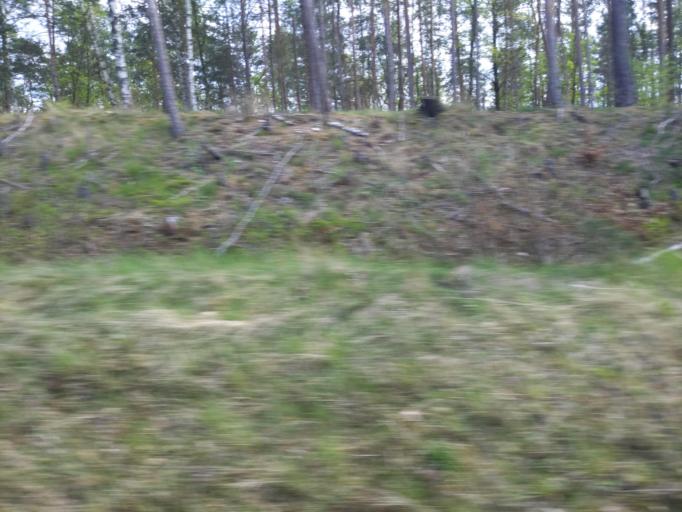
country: DE
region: Saxony
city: Albertstadt
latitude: 51.1276
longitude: 13.8052
